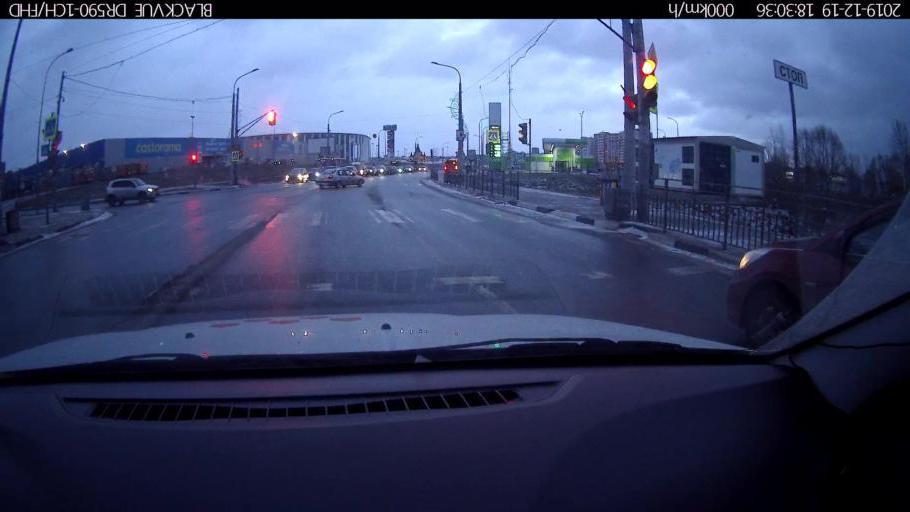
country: RU
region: Nizjnij Novgorod
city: Nizhniy Novgorod
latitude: 56.3361
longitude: 43.9556
